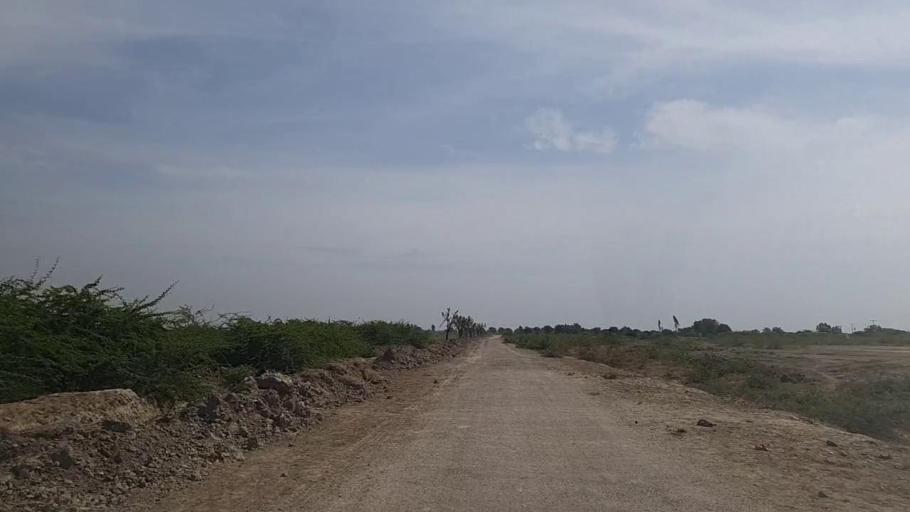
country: PK
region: Sindh
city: Samaro
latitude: 25.2037
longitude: 69.4619
